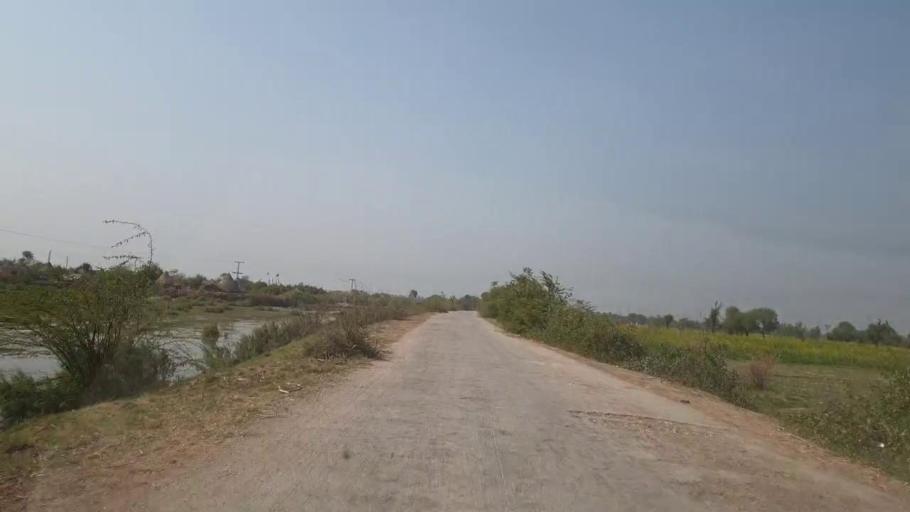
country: PK
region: Sindh
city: Mirpur Khas
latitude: 25.7007
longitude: 69.1410
